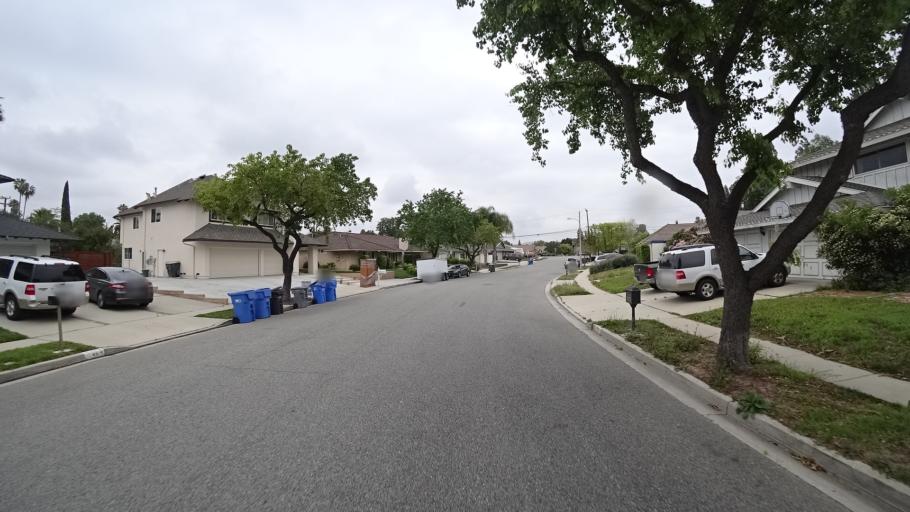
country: US
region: California
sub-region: Ventura County
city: Thousand Oaks
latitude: 34.2090
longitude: -118.8812
